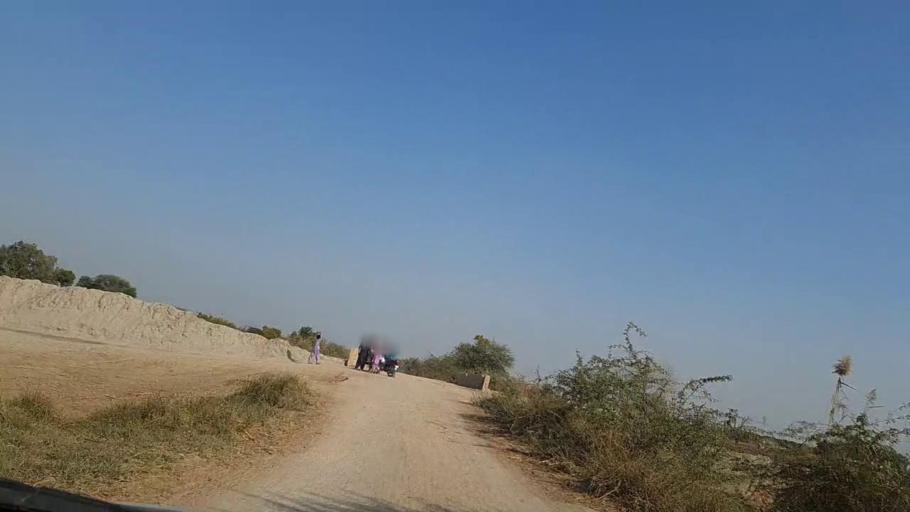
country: PK
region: Sindh
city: Sakrand
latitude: 26.0206
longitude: 68.3294
